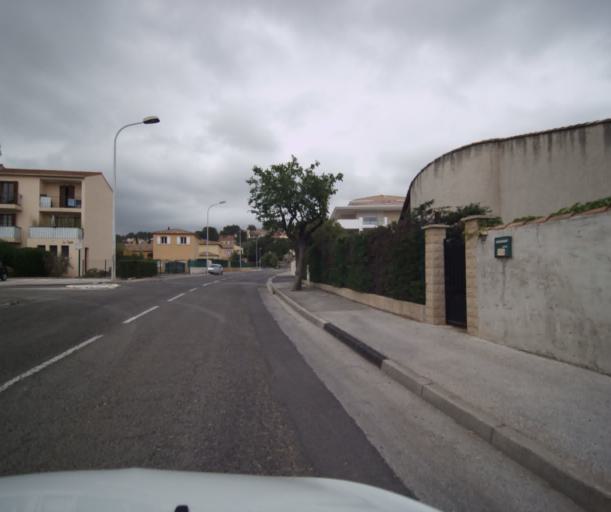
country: FR
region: Provence-Alpes-Cote d'Azur
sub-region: Departement du Var
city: La Garde
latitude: 43.1227
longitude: 6.0011
